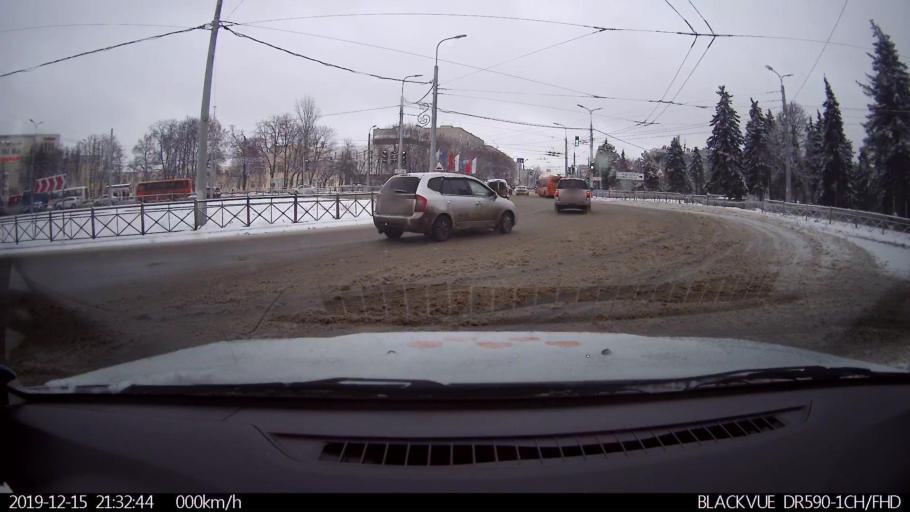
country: RU
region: Nizjnij Novgorod
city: Gorbatovka
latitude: 56.2415
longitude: 43.8627
